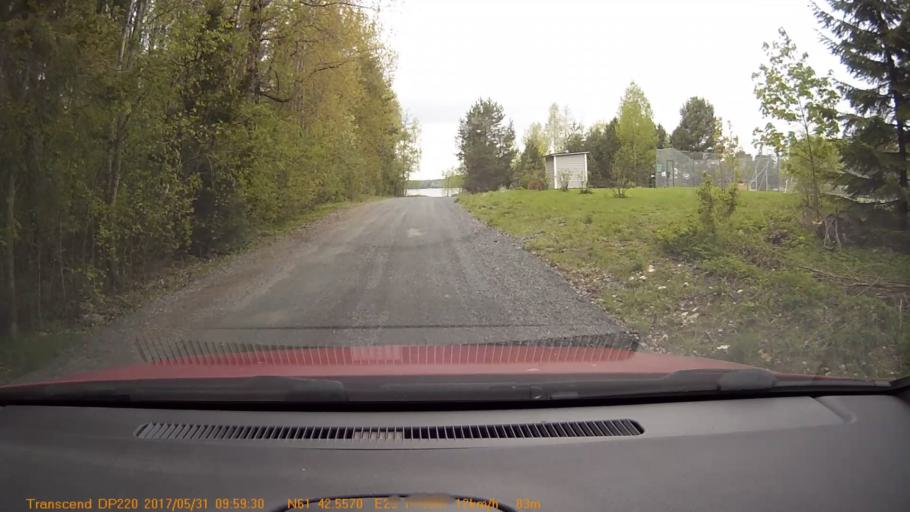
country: FI
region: Pirkanmaa
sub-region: Tampere
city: Viljakkala
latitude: 61.7093
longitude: 23.2394
